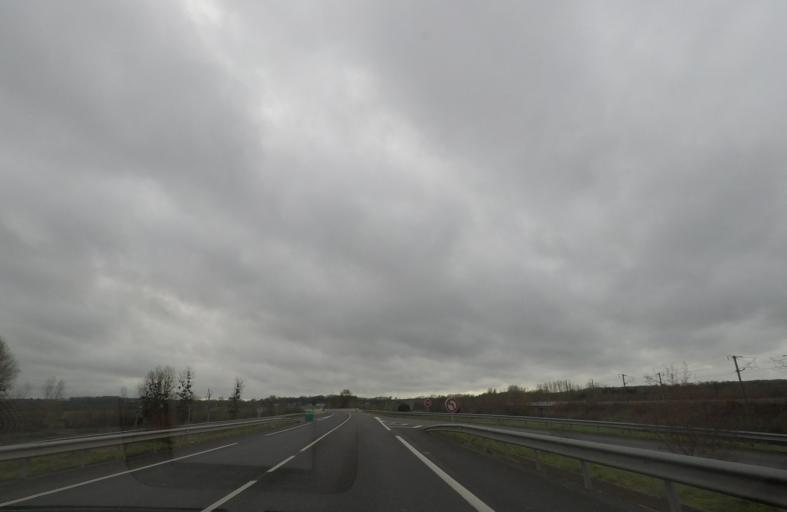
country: FR
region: Centre
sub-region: Departement du Loir-et-Cher
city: Villiers-sur-Loir
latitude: 47.7860
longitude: 1.0051
